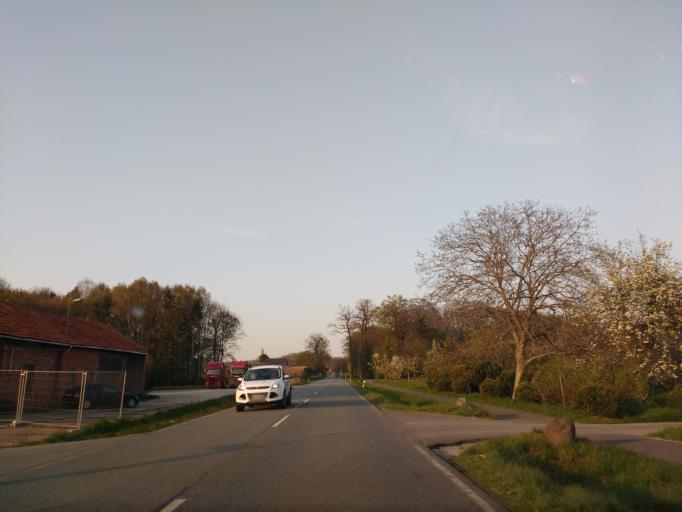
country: DE
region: Lower Saxony
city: Dissen
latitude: 52.0718
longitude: 8.2309
